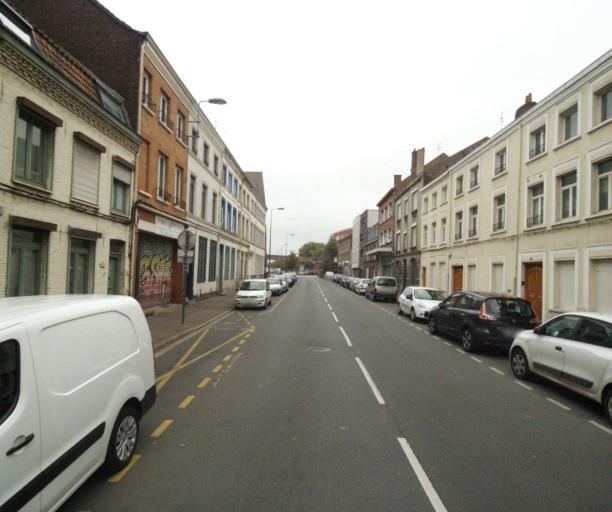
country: FR
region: Nord-Pas-de-Calais
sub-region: Departement du Nord
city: Lille
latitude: 50.6193
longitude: 3.0646
